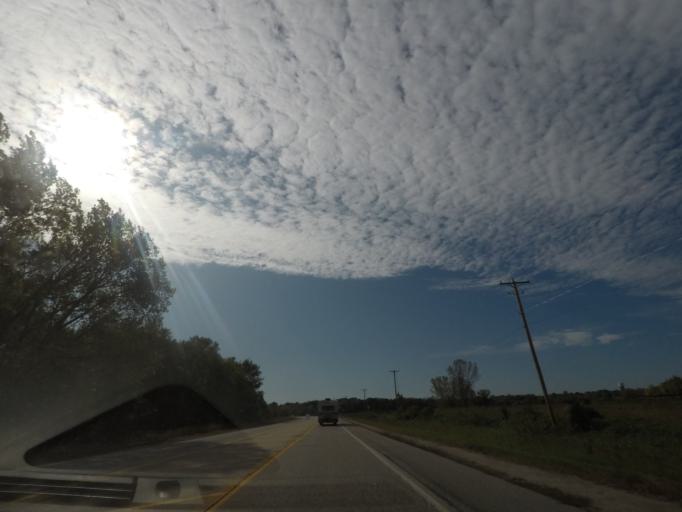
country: US
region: Iowa
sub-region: Story County
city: Ames
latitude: 42.0696
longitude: -93.6225
